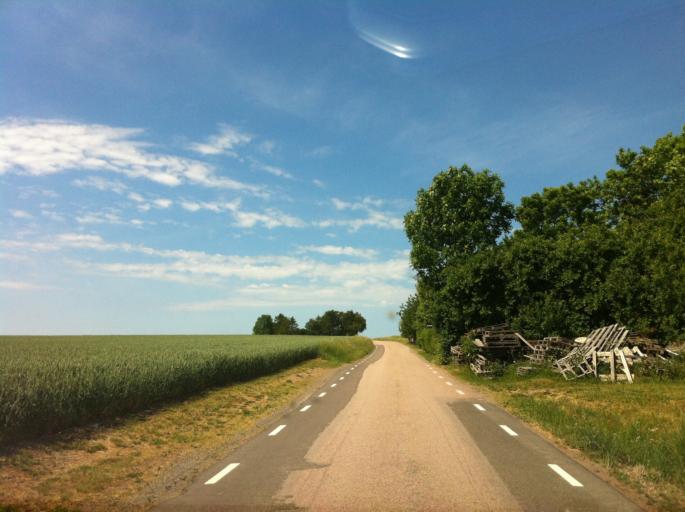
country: SE
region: Skane
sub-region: Landskrona
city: Asmundtorp
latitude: 55.9415
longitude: 12.9138
